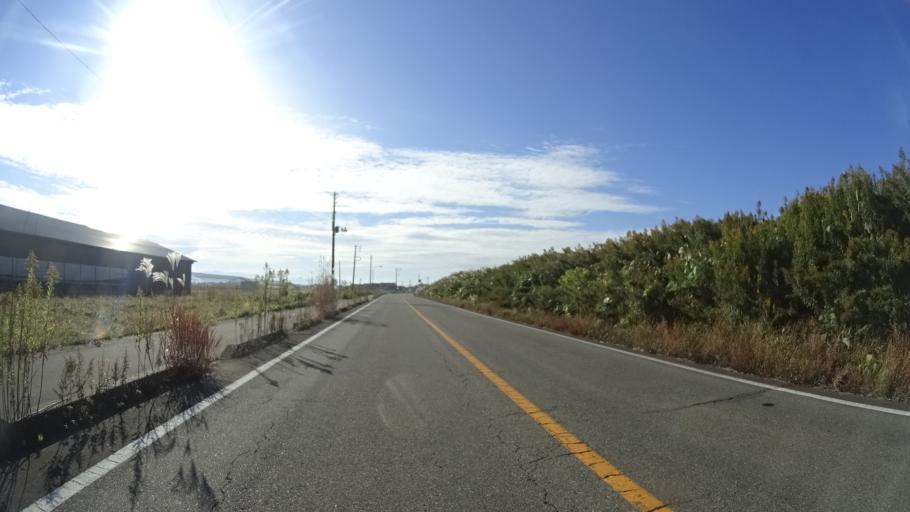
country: JP
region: Niigata
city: Yoshida-kasugacho
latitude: 37.5843
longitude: 138.8350
